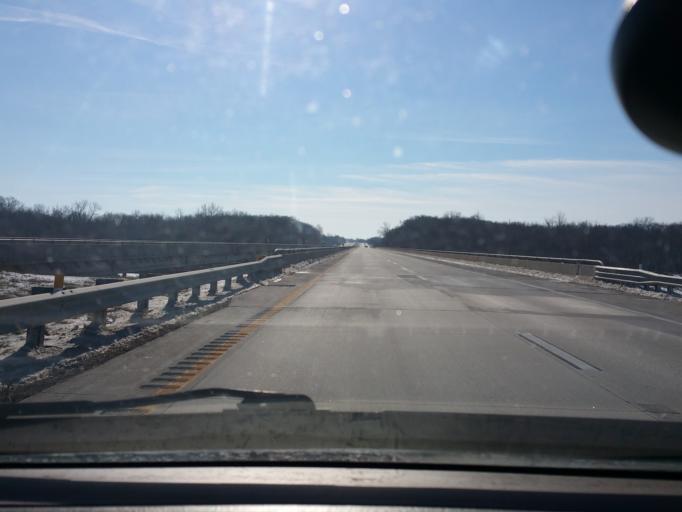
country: US
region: Missouri
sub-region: Daviess County
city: Gallatin
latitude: 40.0263
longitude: -94.0958
